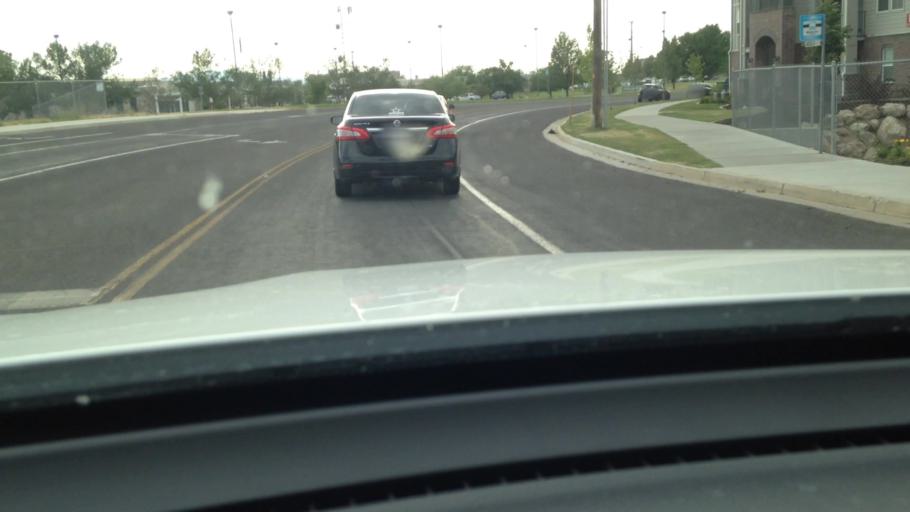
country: US
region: Utah
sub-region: Davis County
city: Farmington
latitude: 40.9805
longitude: -111.9016
